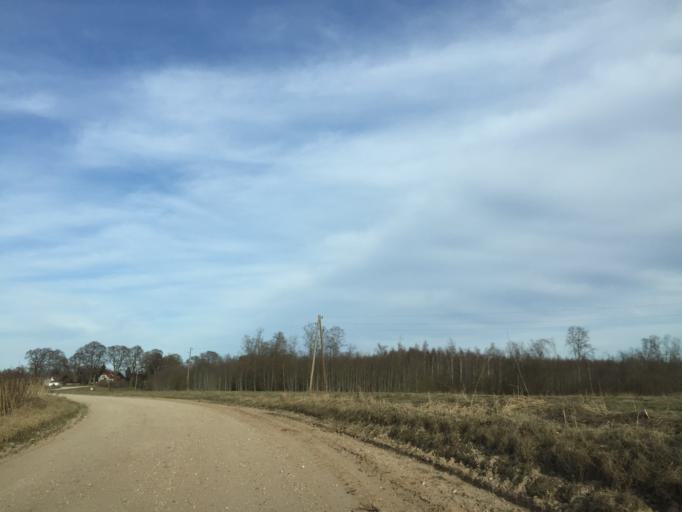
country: LV
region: Kegums
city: Kegums
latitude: 56.7980
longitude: 24.7403
